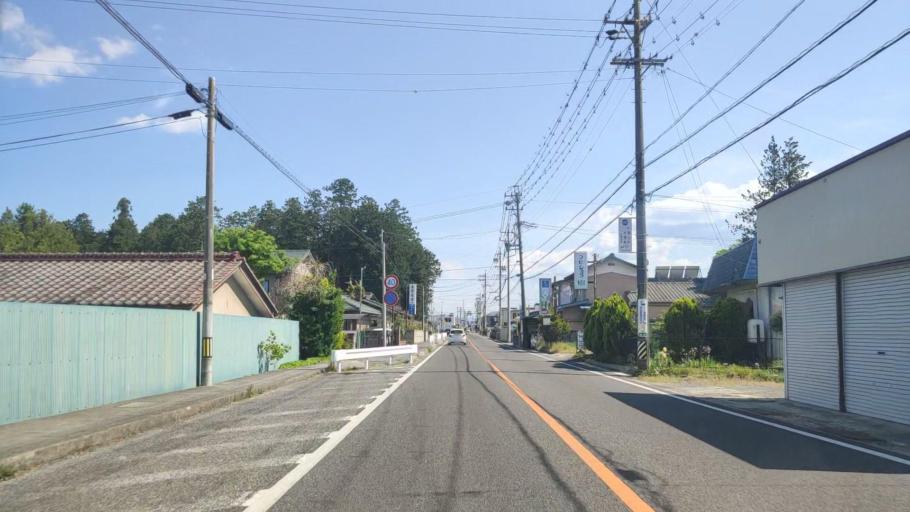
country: JP
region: Nagano
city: Toyoshina
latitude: 36.2933
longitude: 137.9063
